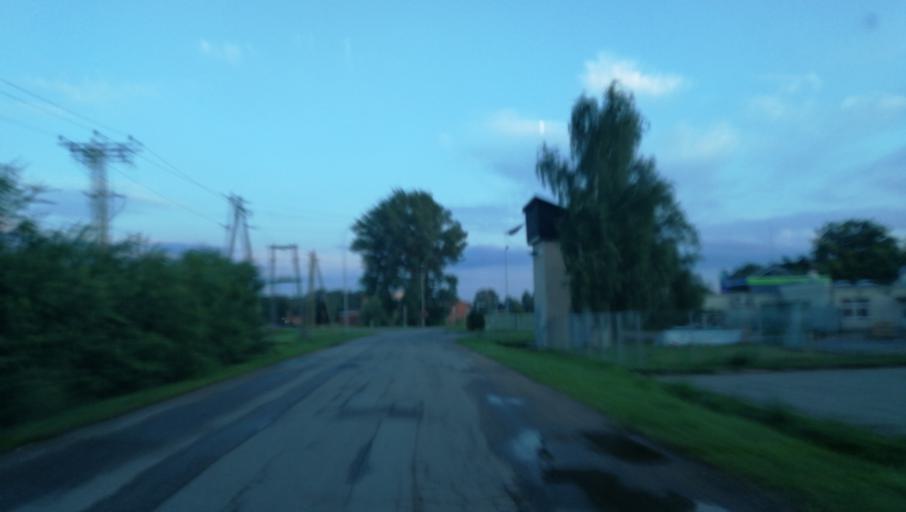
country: LV
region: Cesu Rajons
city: Cesis
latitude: 57.3131
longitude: 25.3053
